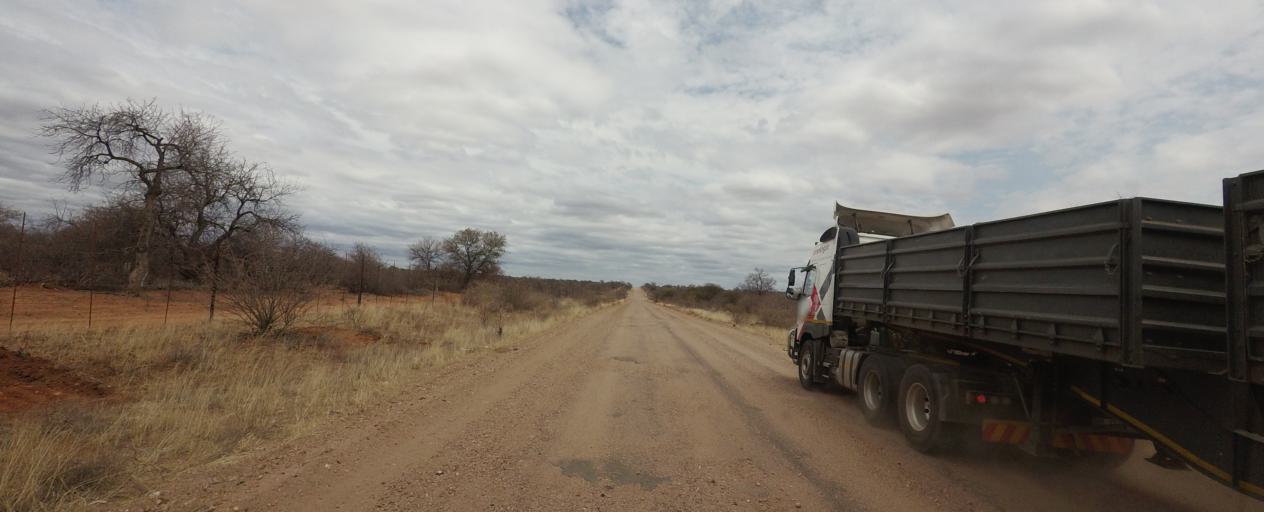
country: BW
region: Central
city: Mathathane
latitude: -22.6749
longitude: 28.6735
